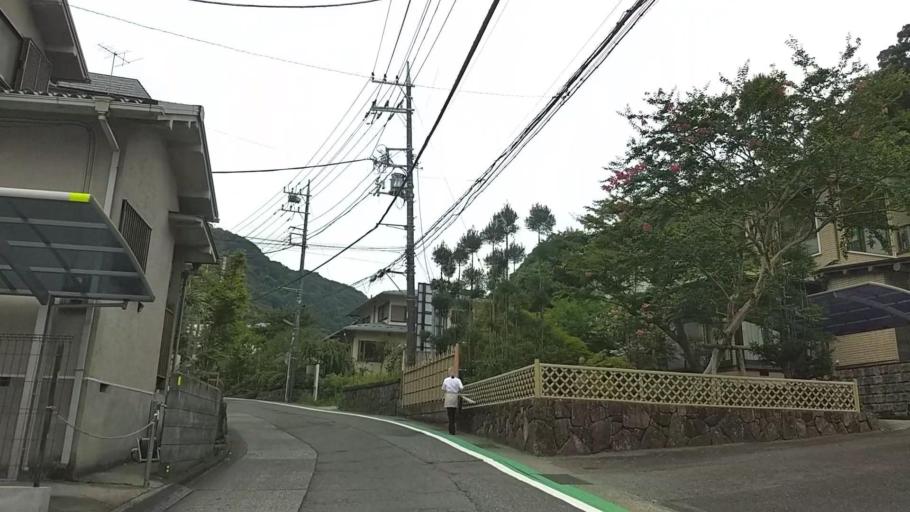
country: JP
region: Kanagawa
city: Odawara
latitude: 35.2318
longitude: 139.1079
